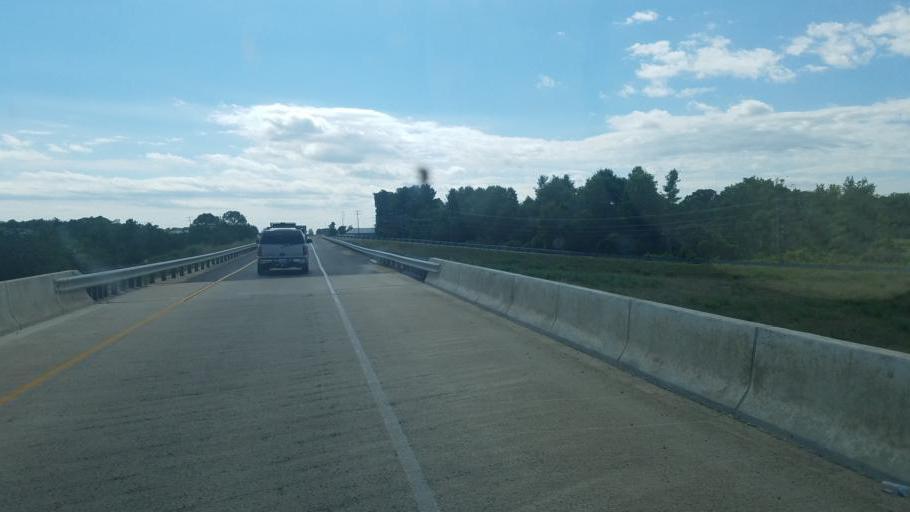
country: US
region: Virginia
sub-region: Fauquier County
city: Bealeton
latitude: 38.6142
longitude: -77.8003
